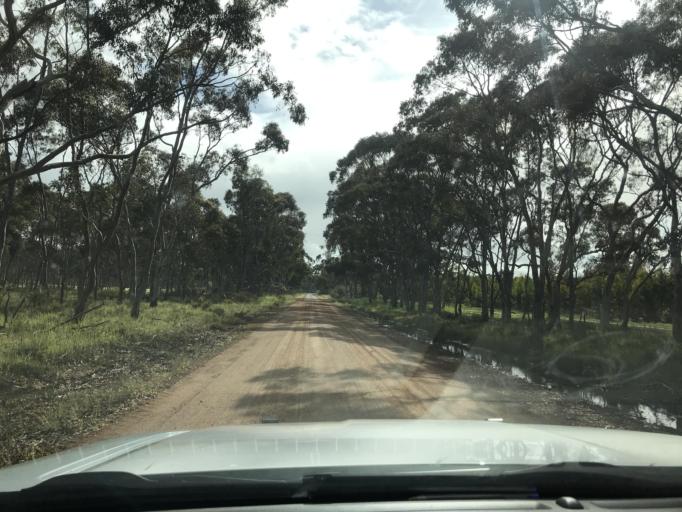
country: AU
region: South Australia
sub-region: Wattle Range
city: Penola
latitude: -37.1865
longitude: 141.1961
